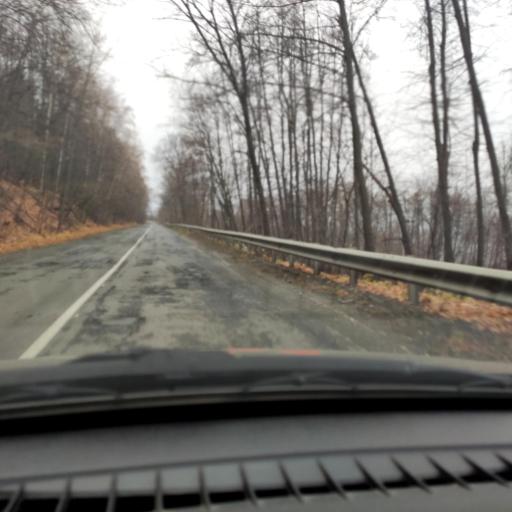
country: RU
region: Samara
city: Povolzhskiy
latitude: 53.4387
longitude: 49.6896
